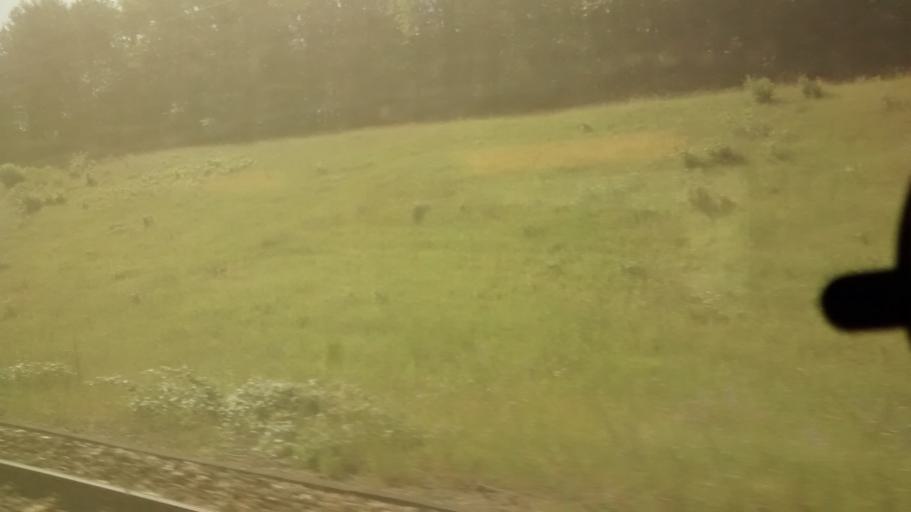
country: FR
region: Pays de la Loire
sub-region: Departement de la Sarthe
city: Connerre
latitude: 48.0457
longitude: 0.5112
